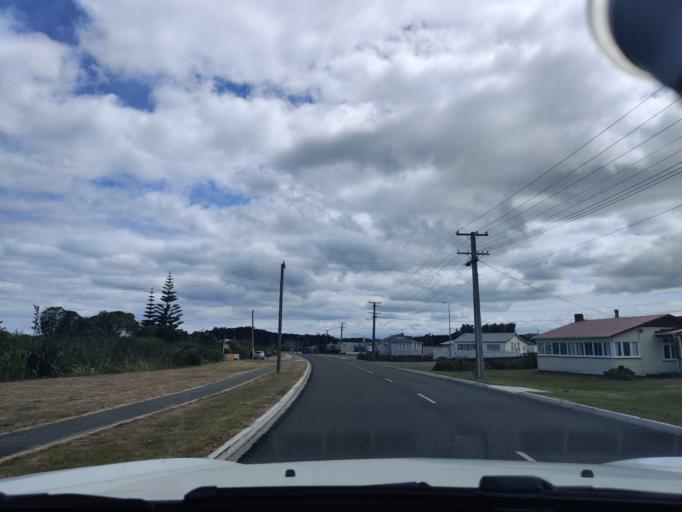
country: NZ
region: Manawatu-Wanganui
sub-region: Horowhenua District
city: Foxton
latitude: -40.4635
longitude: 175.2257
